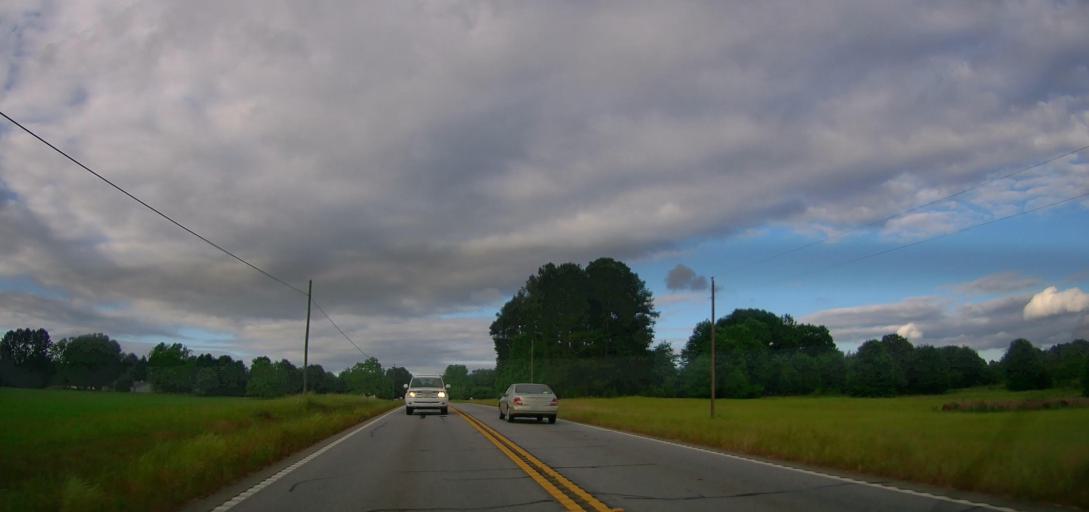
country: US
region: Georgia
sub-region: Oconee County
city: Watkinsville
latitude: 33.8378
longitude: -83.4292
